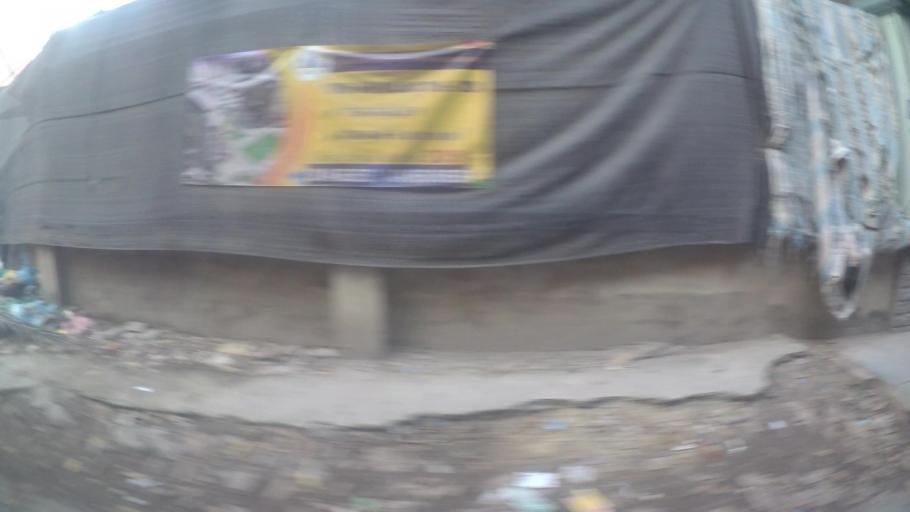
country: VN
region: Ha Noi
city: Cau Giay
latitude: 21.0495
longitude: 105.7940
